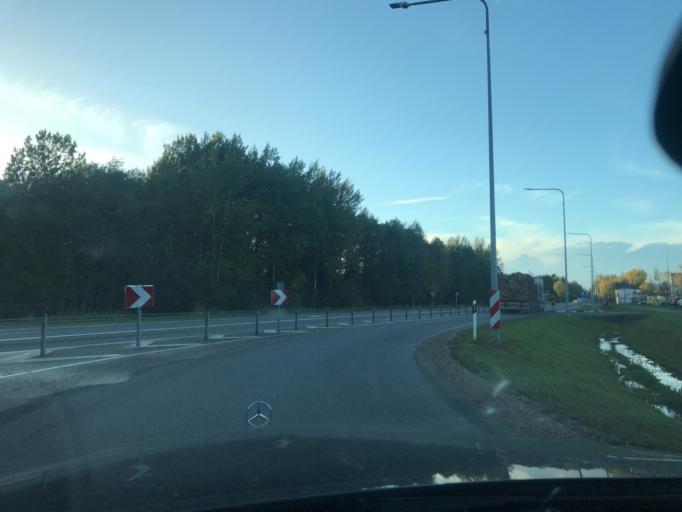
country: EE
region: Vorumaa
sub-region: Voru linn
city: Voru
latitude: 57.8574
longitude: 26.9767
